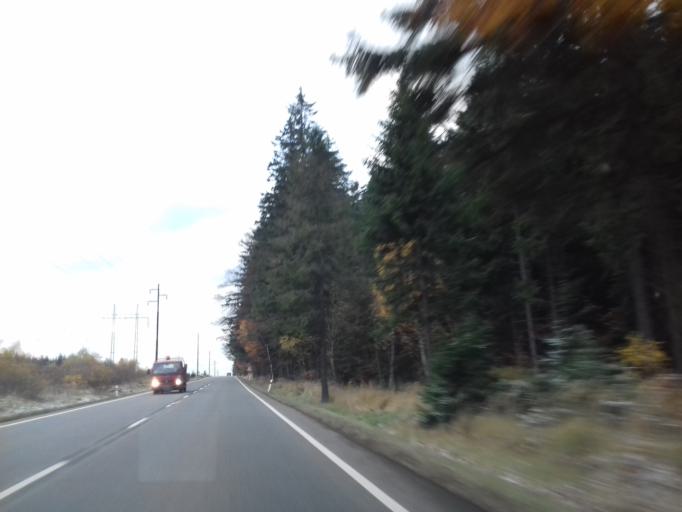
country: CZ
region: Pardubicky
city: Prosec
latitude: 49.7588
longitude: 16.1217
